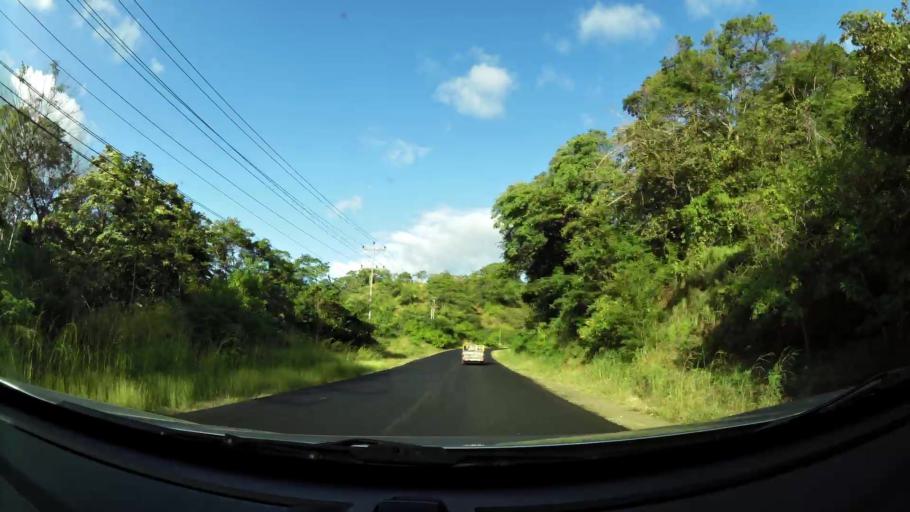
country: CR
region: Guanacaste
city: Sardinal
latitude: 10.5379
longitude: -85.6731
